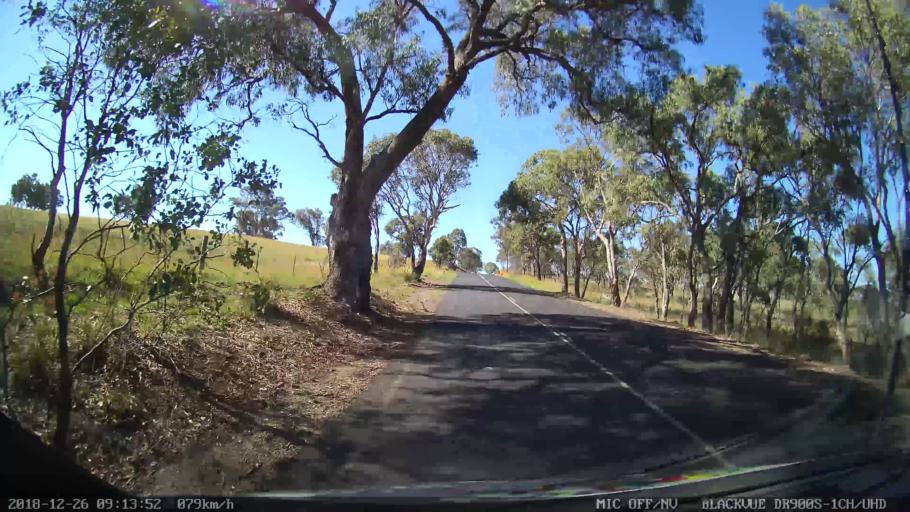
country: AU
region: New South Wales
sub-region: Mid-Western Regional
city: Kandos
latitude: -32.7723
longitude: 149.9801
